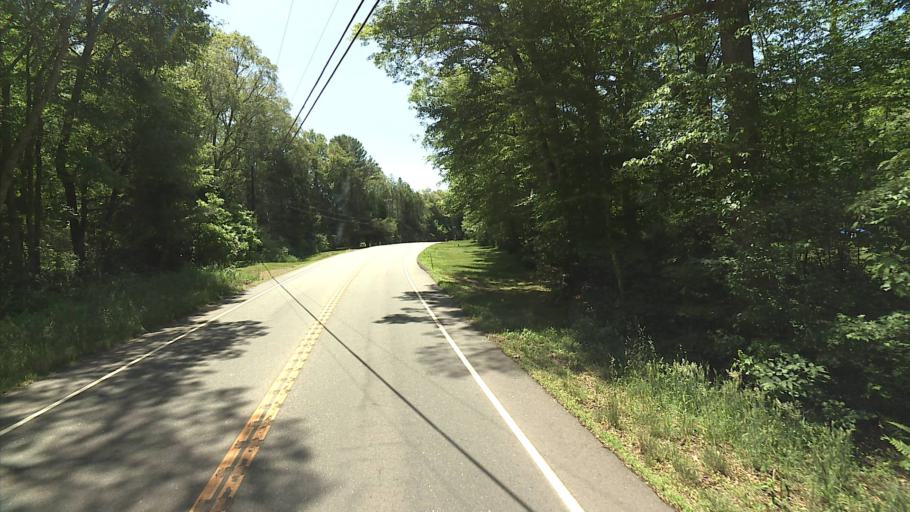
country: US
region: Rhode Island
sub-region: Washington County
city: Hopkinton
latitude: 41.5324
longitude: -71.8370
